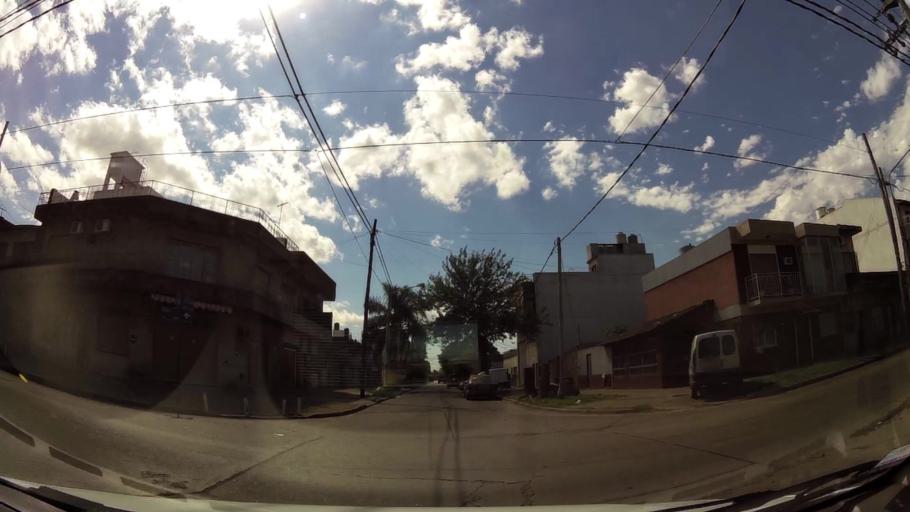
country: AR
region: Buenos Aires
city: San Justo
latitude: -34.6566
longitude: -58.5358
